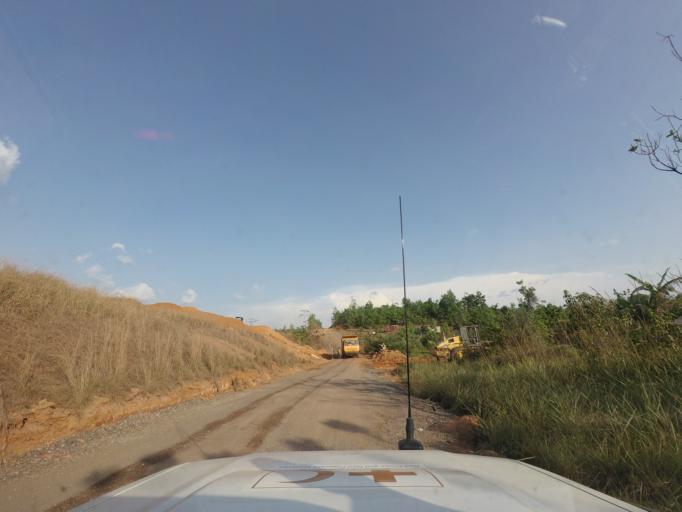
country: LR
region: Bong
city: Gbarnga
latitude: 7.0270
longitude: -9.5023
